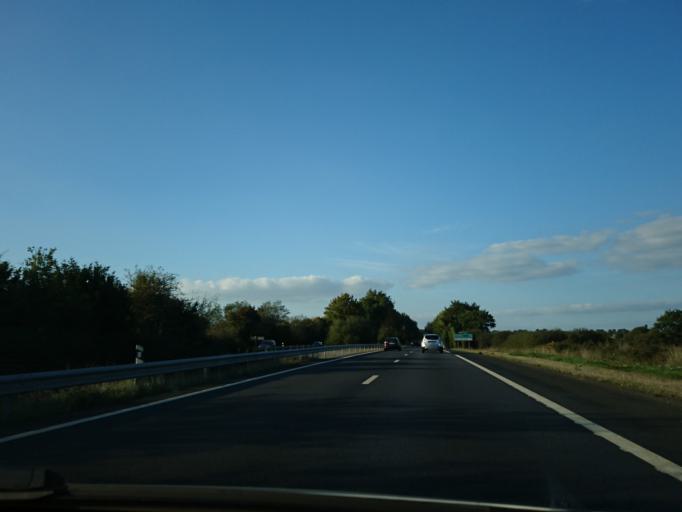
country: FR
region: Brittany
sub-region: Departement d'Ille-et-Vilaine
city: Grand-Fougeray
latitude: 47.7081
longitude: -1.7050
